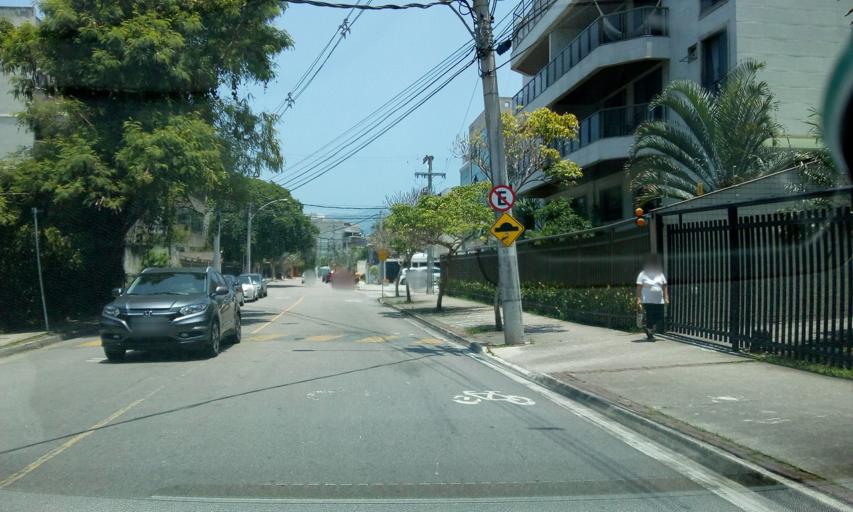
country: BR
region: Rio de Janeiro
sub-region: Nilopolis
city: Nilopolis
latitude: -23.0217
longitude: -43.4620
